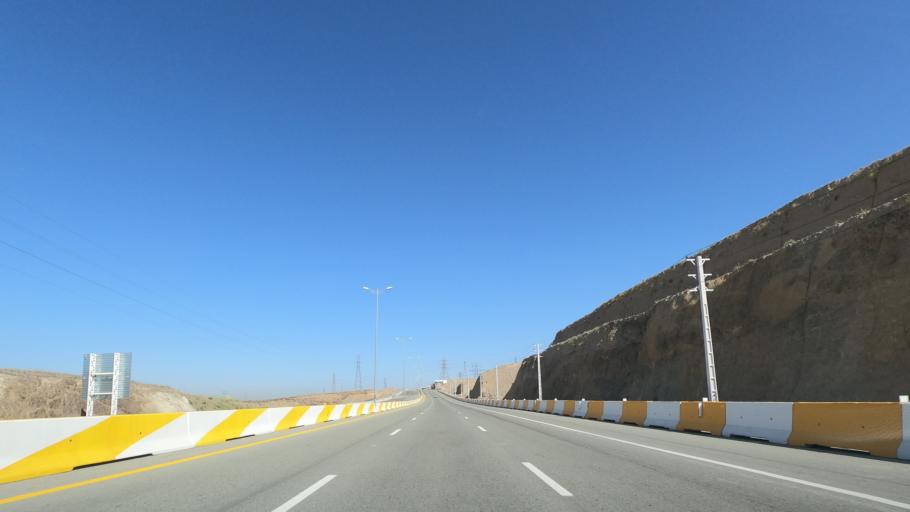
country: IR
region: Tehran
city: Shahr-e Qods
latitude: 35.7712
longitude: 51.0594
